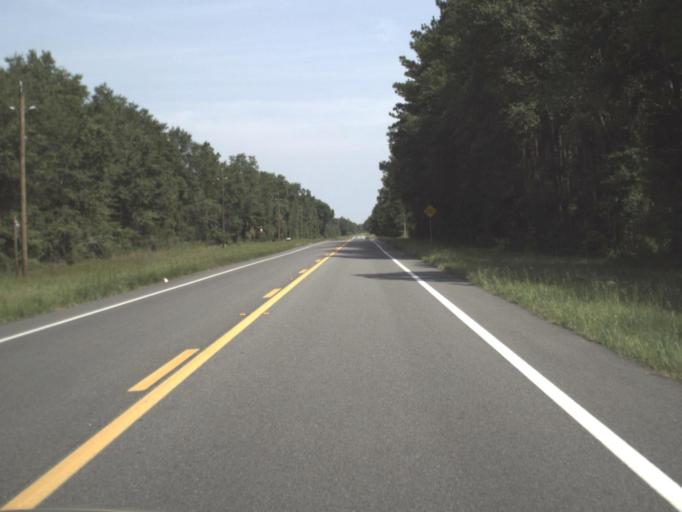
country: US
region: Florida
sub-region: Hamilton County
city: Jasper
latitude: 30.5998
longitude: -83.0134
